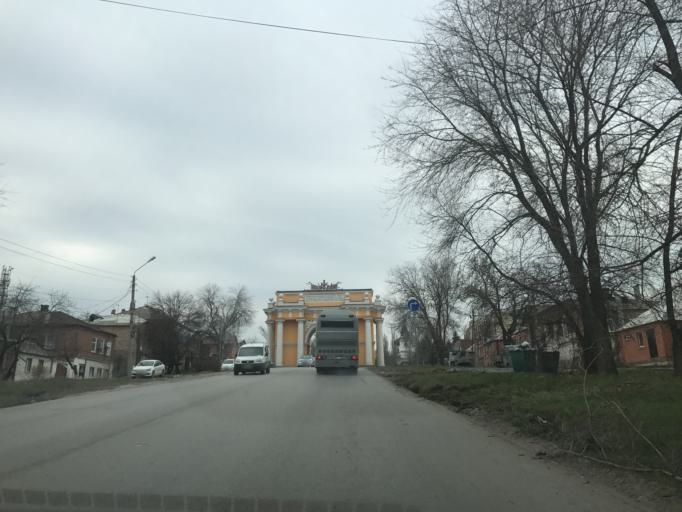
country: RU
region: Rostov
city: Novocherkassk
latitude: 47.4045
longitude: 40.0832
